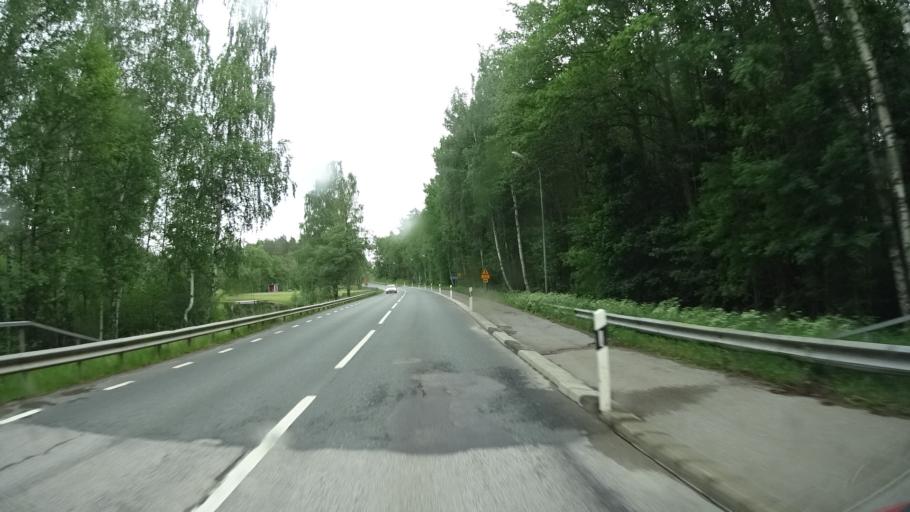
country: SE
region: Kalmar
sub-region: Hultsfreds Kommun
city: Hultsfred
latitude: 57.5465
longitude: 15.7328
